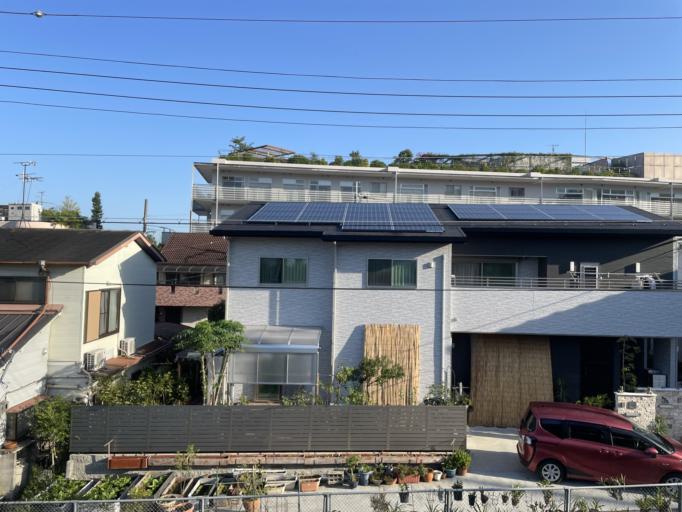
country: JP
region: Osaka
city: Yao
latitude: 34.6277
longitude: 135.6386
